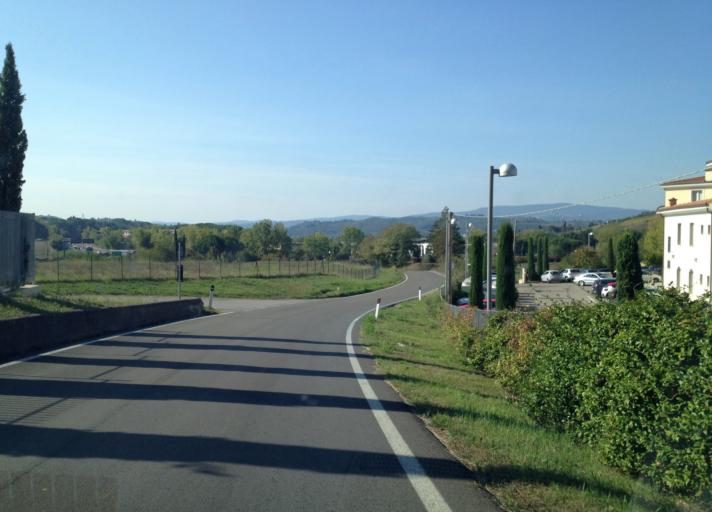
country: IT
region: Tuscany
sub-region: Provincia di Siena
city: Poggibonsi
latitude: 43.4874
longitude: 11.1557
